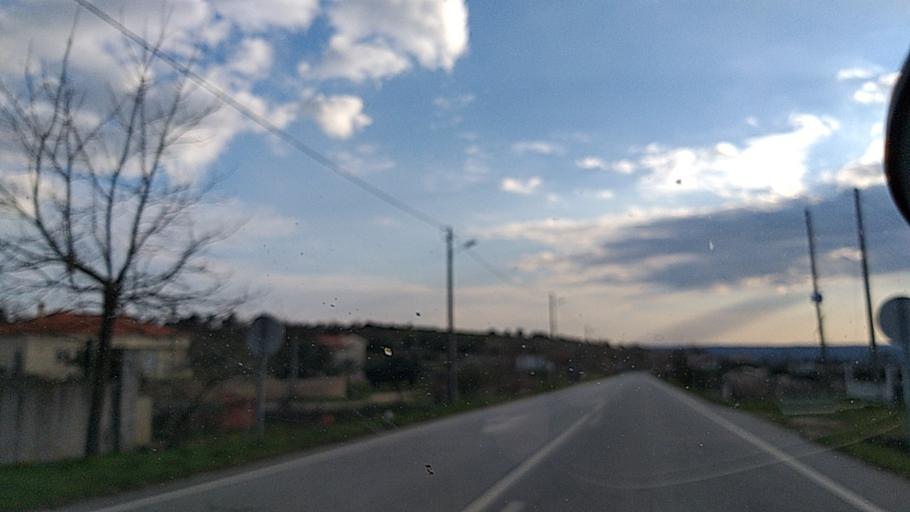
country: ES
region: Castille and Leon
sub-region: Provincia de Salamanca
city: Aldea del Obispo
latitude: 40.7178
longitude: -6.9061
